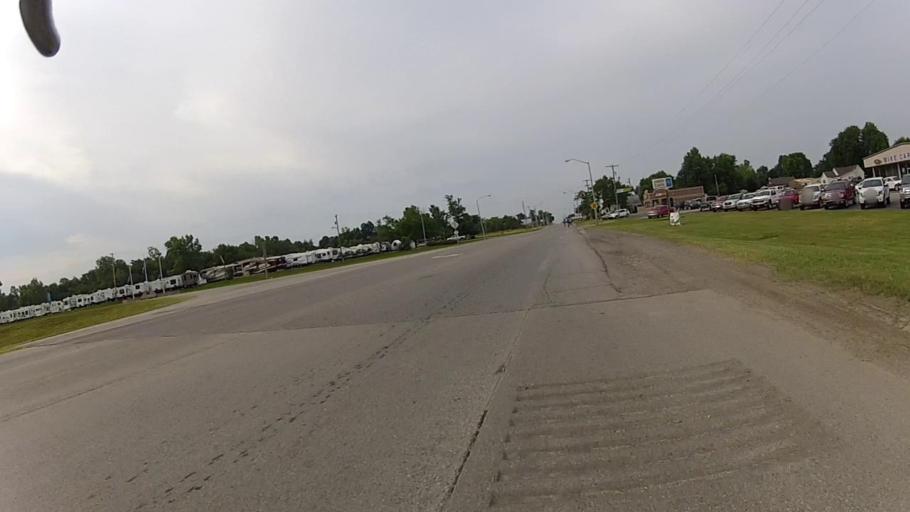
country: US
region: Kansas
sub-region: Cherokee County
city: Columbus
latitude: 37.1781
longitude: -94.8318
